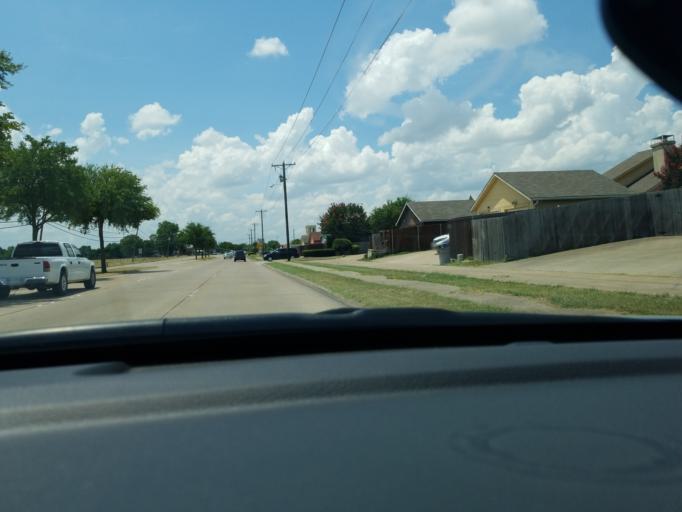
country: US
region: Texas
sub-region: Dallas County
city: Sunnyvale
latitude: 32.8194
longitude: -96.5959
